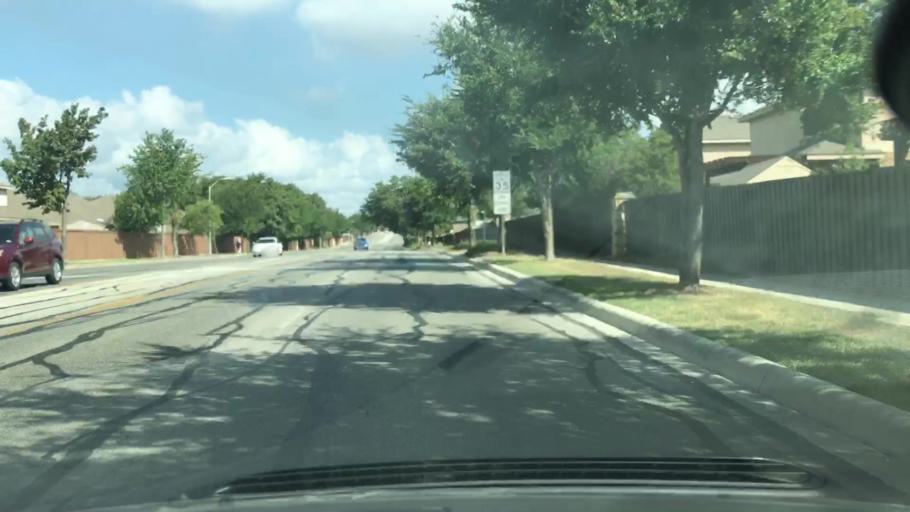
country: US
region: Texas
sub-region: Guadalupe County
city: Cibolo
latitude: 29.5762
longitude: -98.2433
